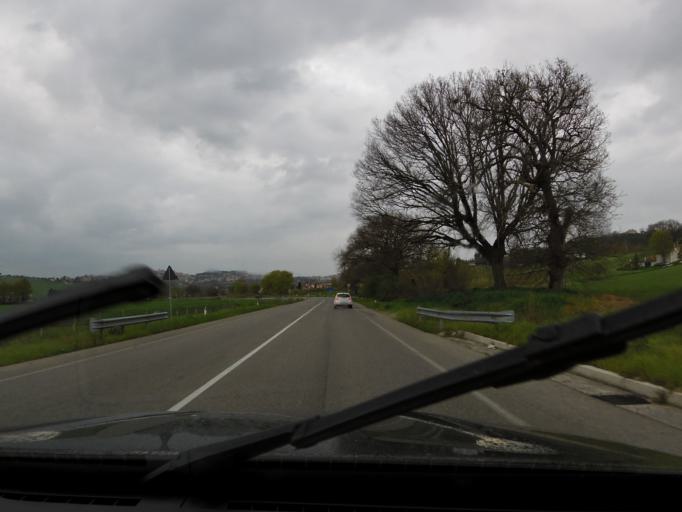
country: IT
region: The Marches
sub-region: Provincia di Ancona
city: Villa Musone
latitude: 43.4574
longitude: 13.5882
